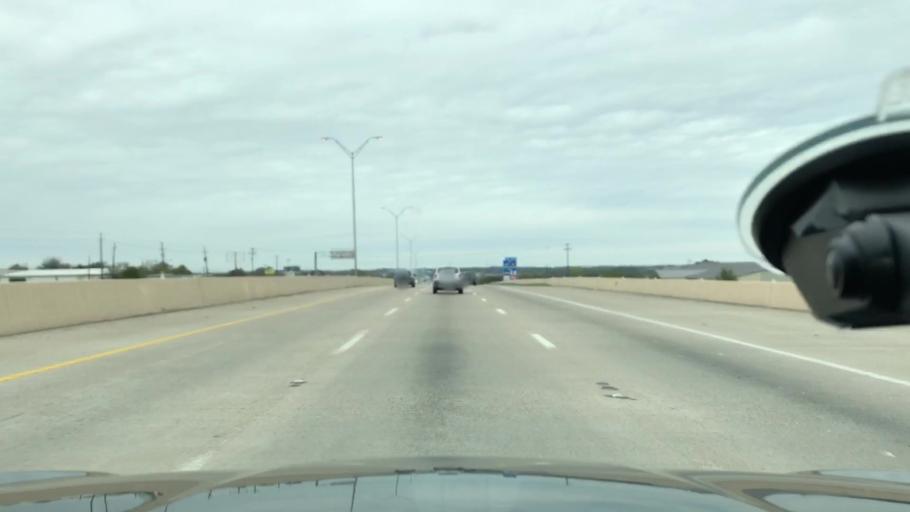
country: US
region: Texas
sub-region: Dallas County
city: DeSoto
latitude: 32.5747
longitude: -96.8223
